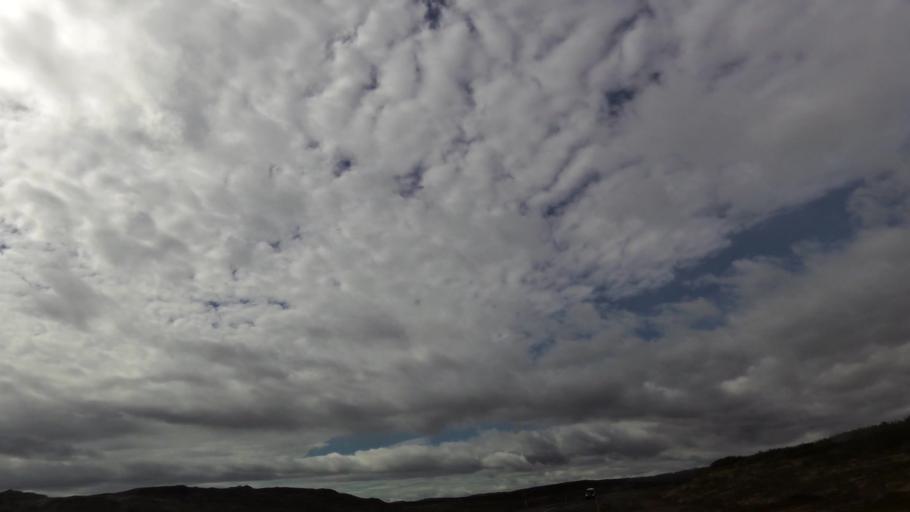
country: IS
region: West
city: Stykkisholmur
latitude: 65.5349
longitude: -22.0906
